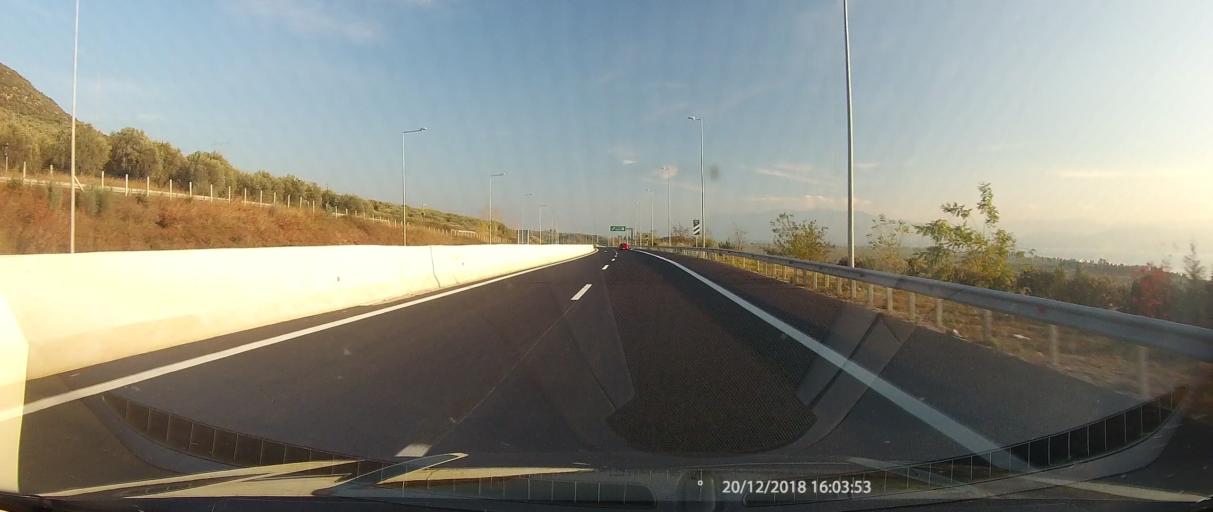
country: GR
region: Central Greece
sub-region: Nomos Fthiotidos
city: Stylida
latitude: 38.9188
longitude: 22.6476
